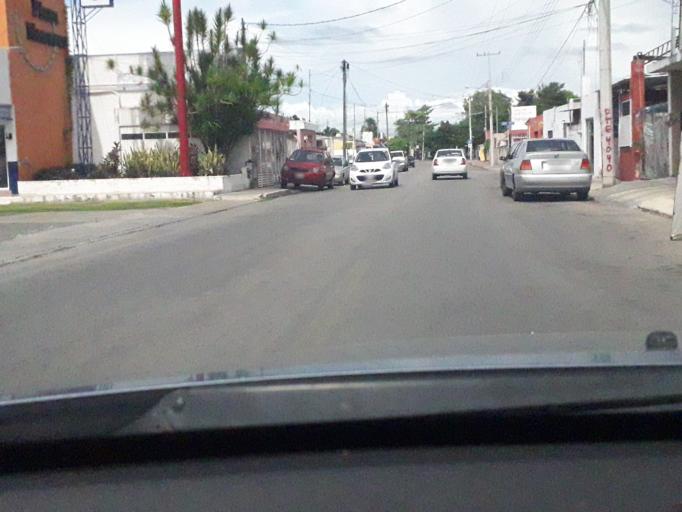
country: MX
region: Yucatan
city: Merida
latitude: 20.9772
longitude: -89.6556
